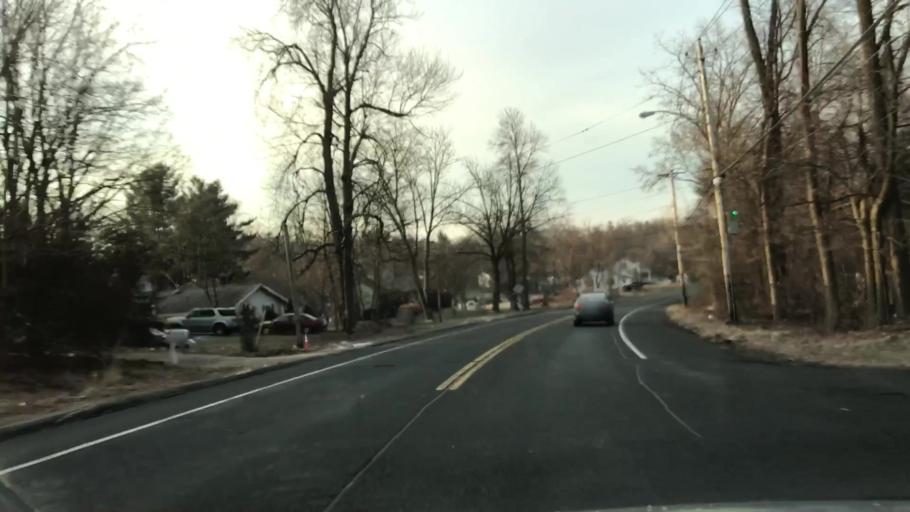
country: US
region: New York
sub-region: Rockland County
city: New Square
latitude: 41.1384
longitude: -74.0358
